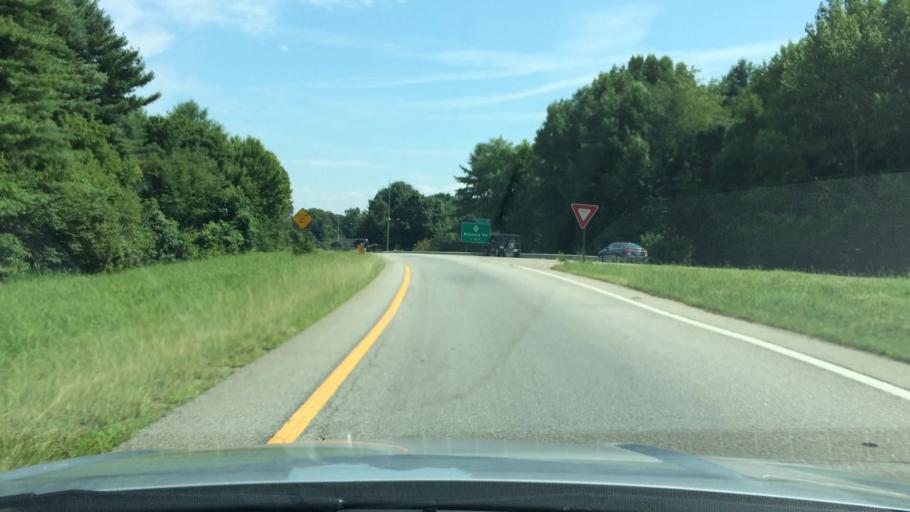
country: US
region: North Carolina
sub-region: Buncombe County
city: Bent Creek
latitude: 35.5557
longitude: -82.6093
